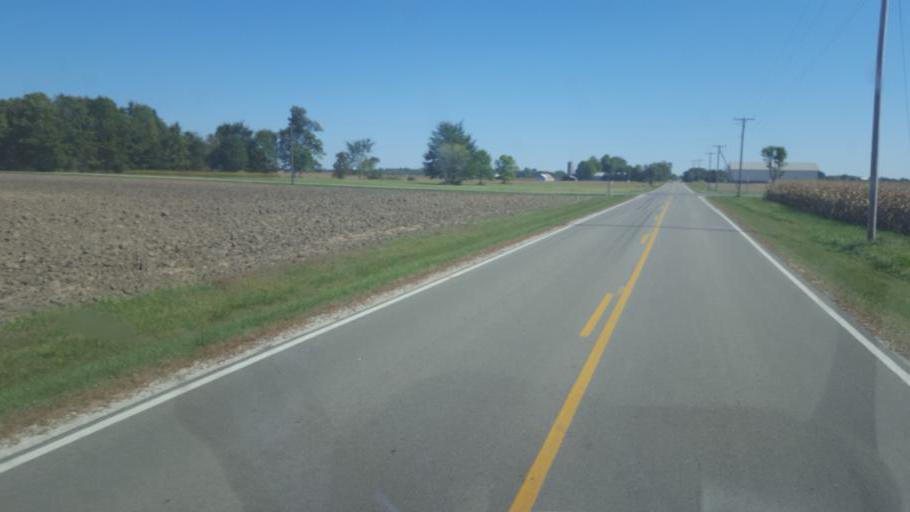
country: US
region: Ohio
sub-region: Crawford County
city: Bucyrus
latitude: 40.8631
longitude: -83.0179
